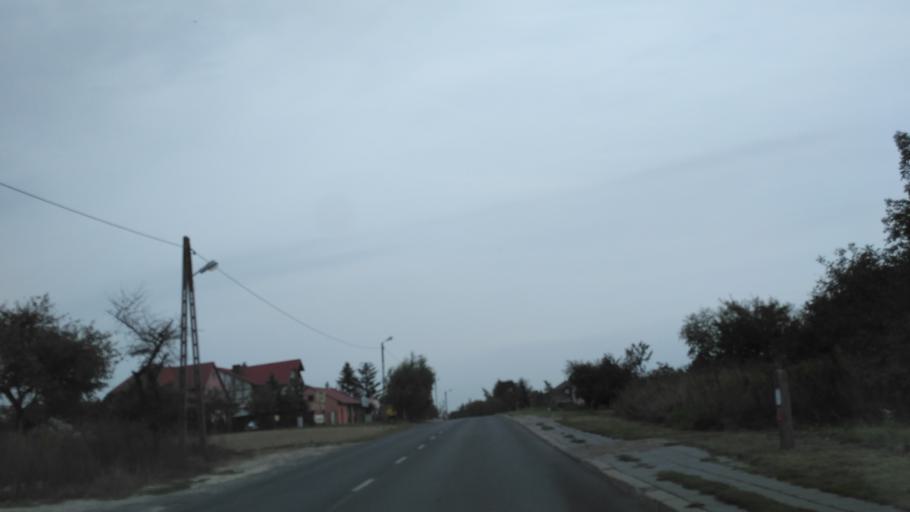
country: PL
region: Lublin Voivodeship
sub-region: Powiat lubelski
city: Lublin
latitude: 51.2168
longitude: 22.5904
